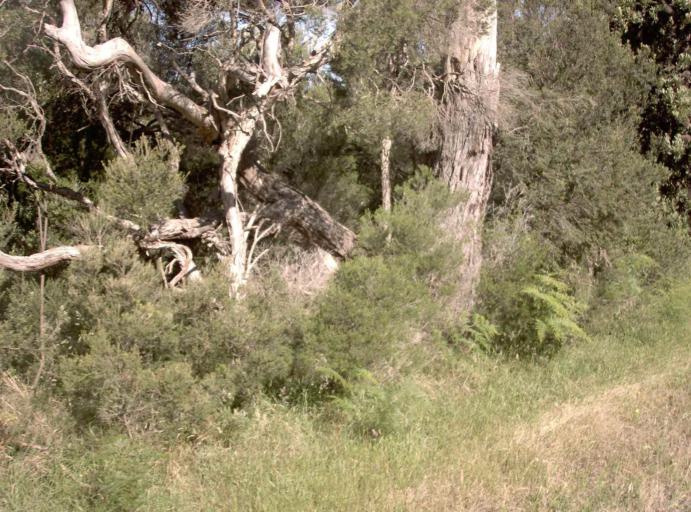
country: AU
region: Victoria
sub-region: Latrobe
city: Traralgon
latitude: -38.6493
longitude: 146.6744
